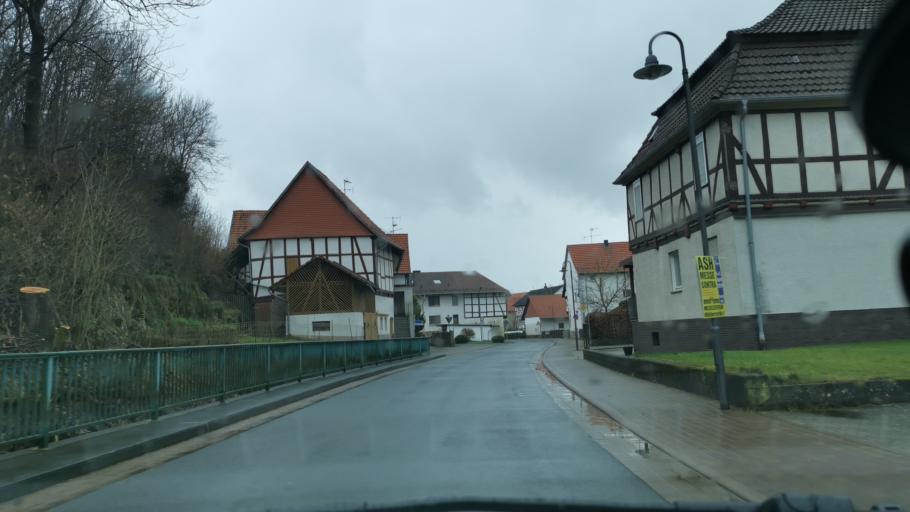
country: DE
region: Hesse
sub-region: Regierungsbezirk Kassel
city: Cornberg
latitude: 51.0599
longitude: 9.8860
